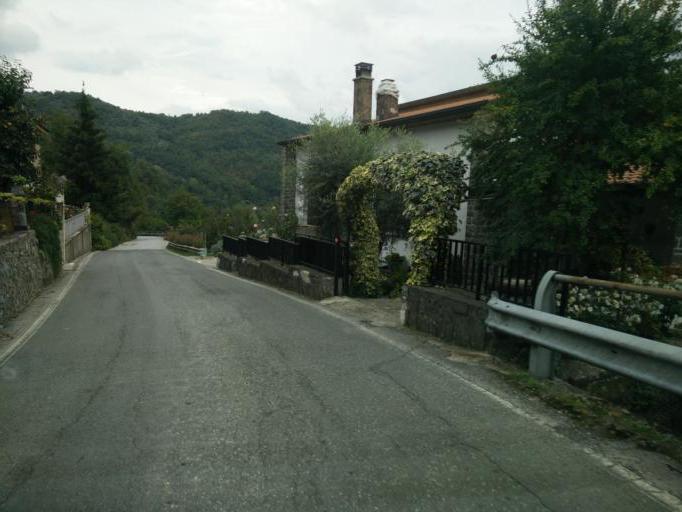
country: IT
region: Tuscany
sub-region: Provincia di Massa-Carrara
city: Fivizzano
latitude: 44.2050
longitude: 10.0944
